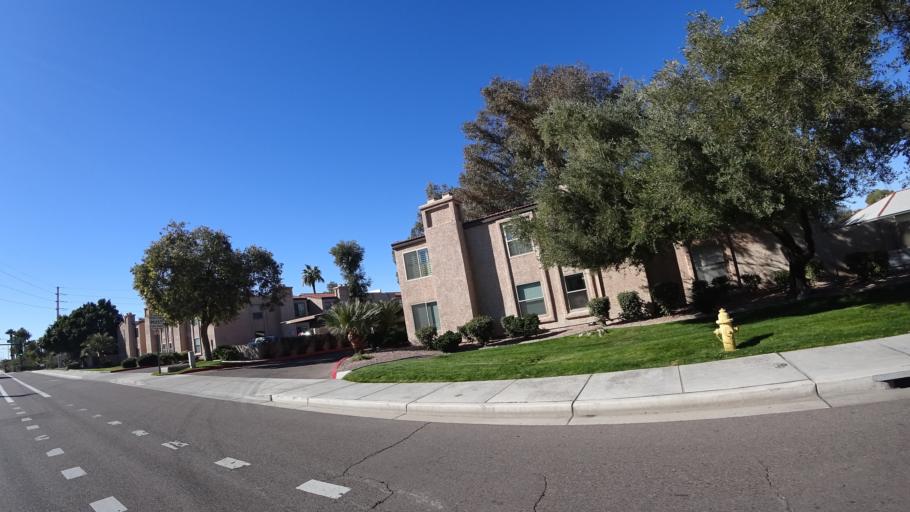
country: US
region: Arizona
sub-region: Maricopa County
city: Paradise Valley
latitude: 33.4737
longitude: -111.9697
